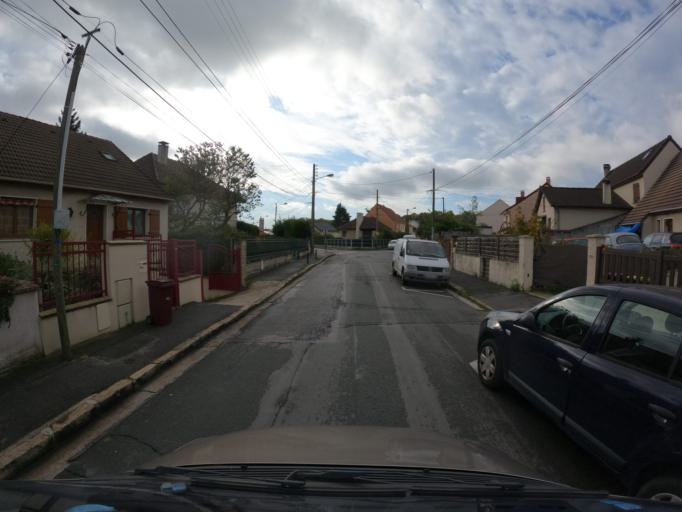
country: FR
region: Ile-de-France
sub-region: Departement de Seine-Saint-Denis
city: Montfermeil
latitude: 48.9015
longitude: 2.5883
